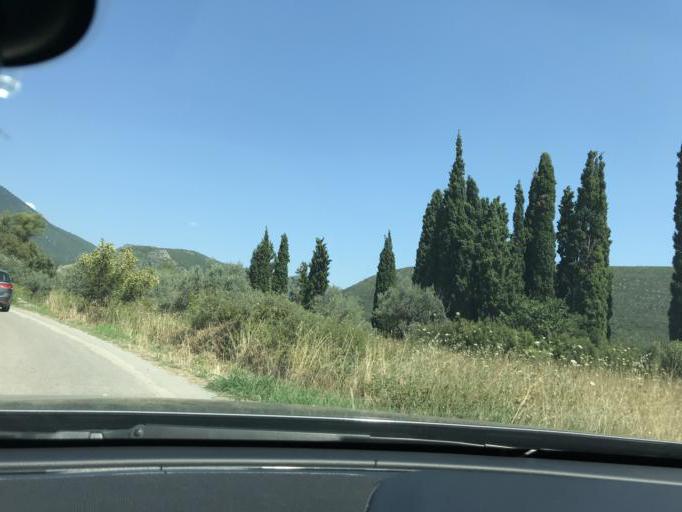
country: GR
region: Central Greece
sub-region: Nomos Fthiotidos
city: Kato Tithorea
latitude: 38.5195
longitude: 22.7466
